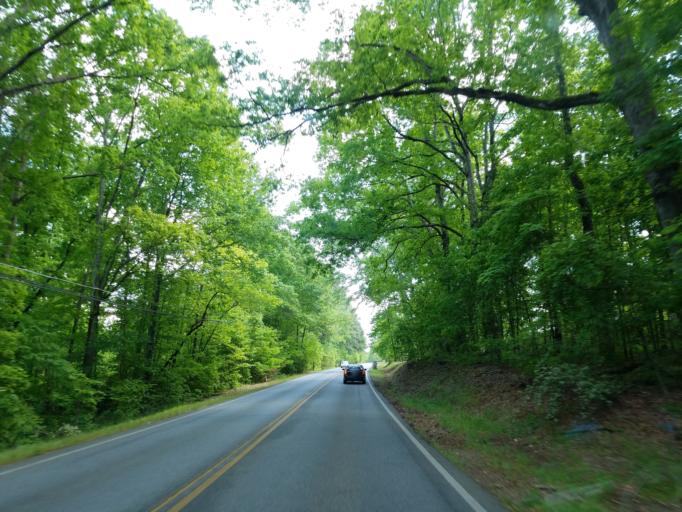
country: US
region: Georgia
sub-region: Monroe County
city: Forsyth
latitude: 33.0651
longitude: -83.9535
